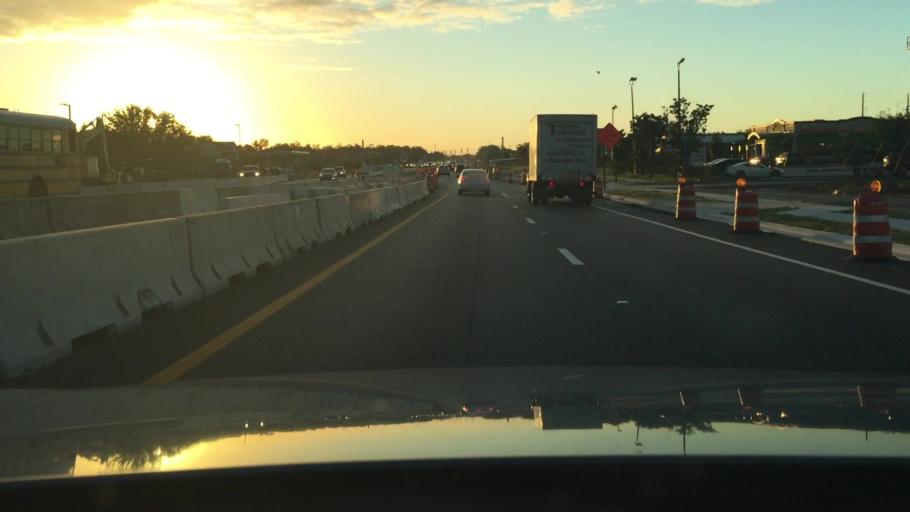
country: US
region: Florida
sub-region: Osceola County
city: Saint Cloud
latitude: 28.2566
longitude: -81.3215
